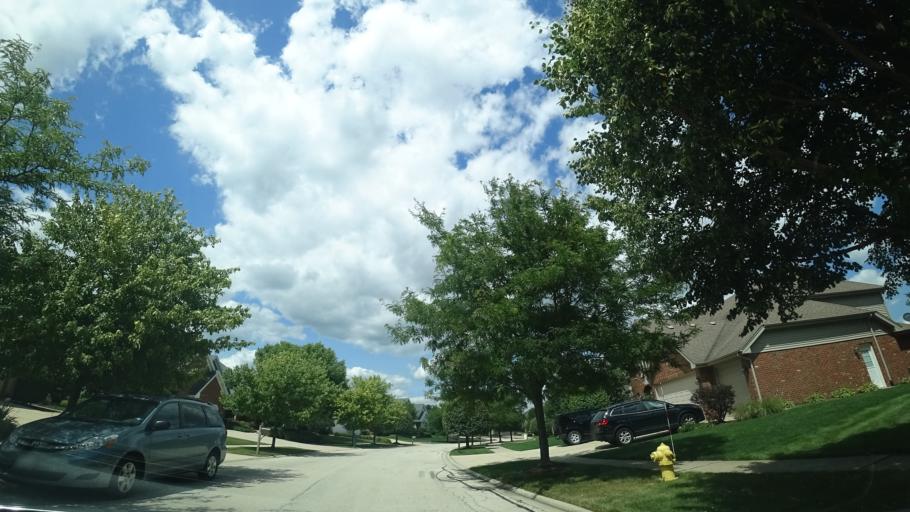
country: US
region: Illinois
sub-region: Will County
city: Homer Glen
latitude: 41.5826
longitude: -87.8971
